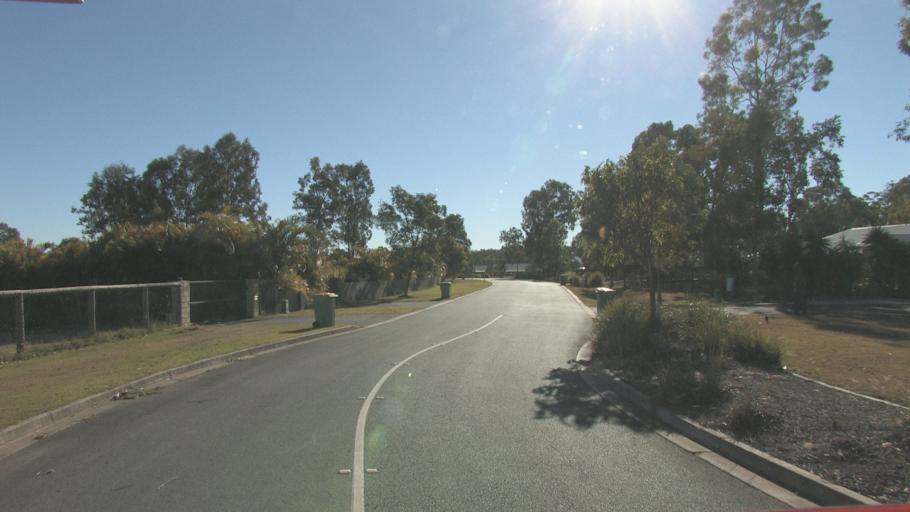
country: AU
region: Queensland
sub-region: Logan
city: North Maclean
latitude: -27.7575
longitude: 152.9667
